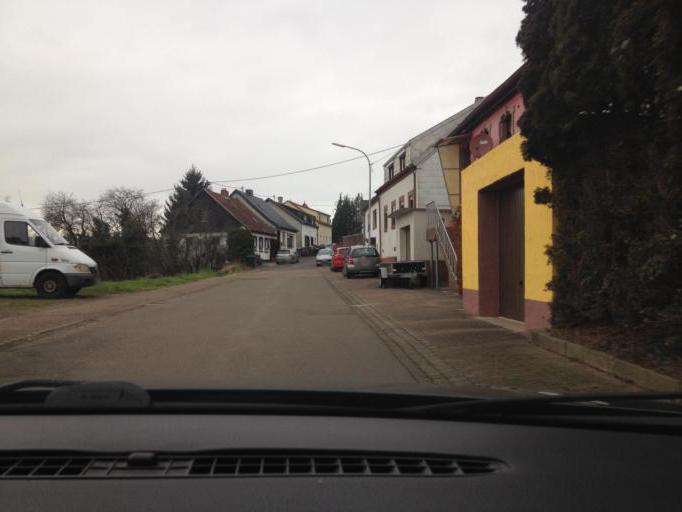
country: DE
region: Saarland
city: Schiffweiler
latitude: 49.3727
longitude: 7.1382
